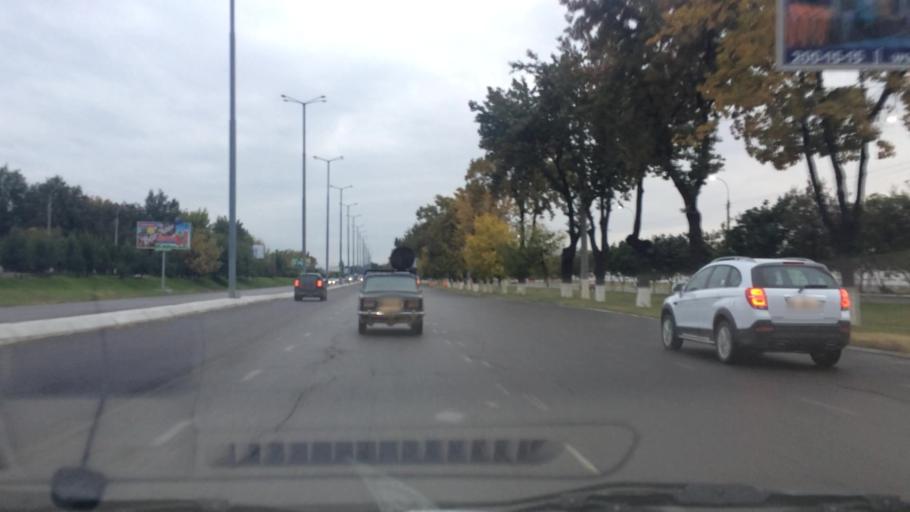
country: UZ
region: Toshkent Shahri
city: Tashkent
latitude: 41.2498
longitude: 69.1821
